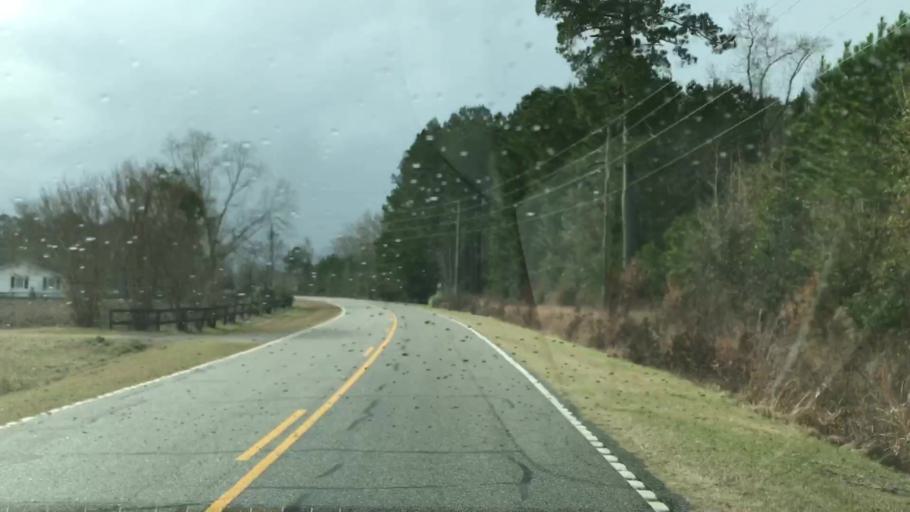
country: US
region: South Carolina
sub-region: Florence County
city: Johnsonville
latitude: 33.6772
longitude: -79.3879
